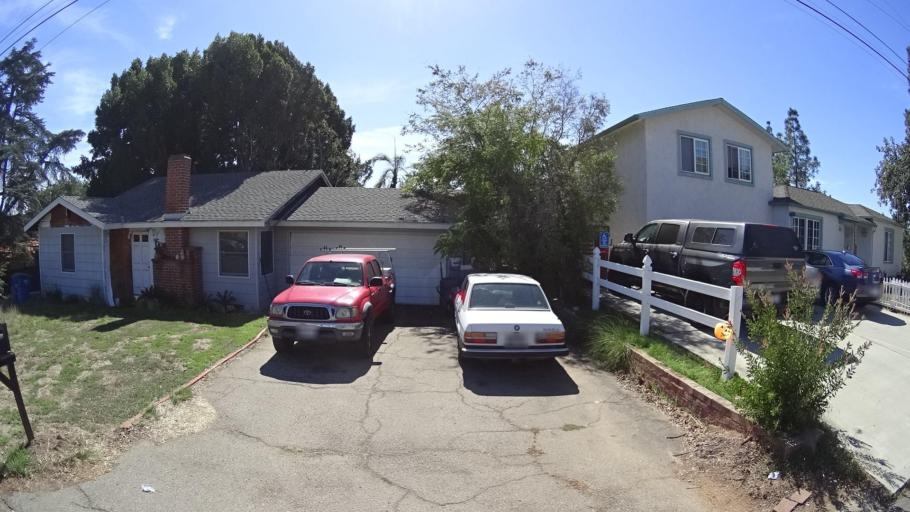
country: US
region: California
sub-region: San Diego County
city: Casa de Oro-Mount Helix
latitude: 32.7555
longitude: -116.9644
